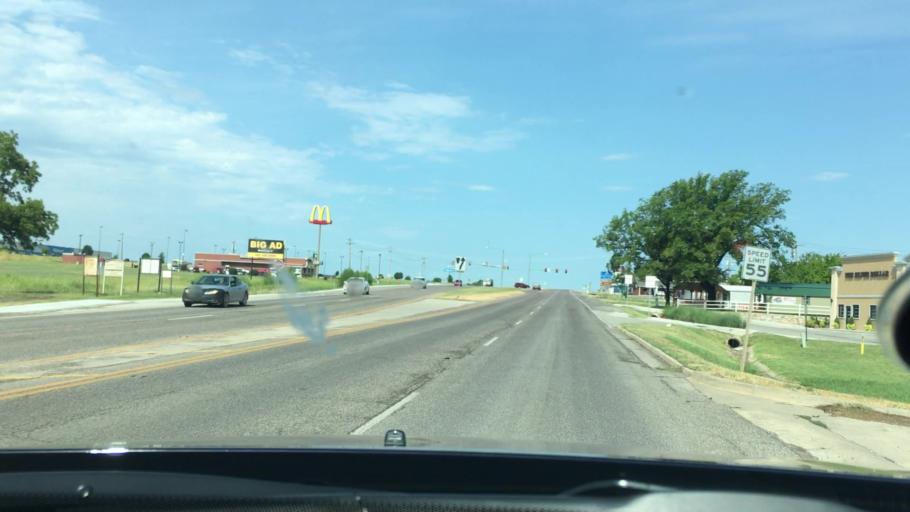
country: US
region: Oklahoma
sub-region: Murray County
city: Sulphur
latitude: 34.5064
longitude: -97.0000
